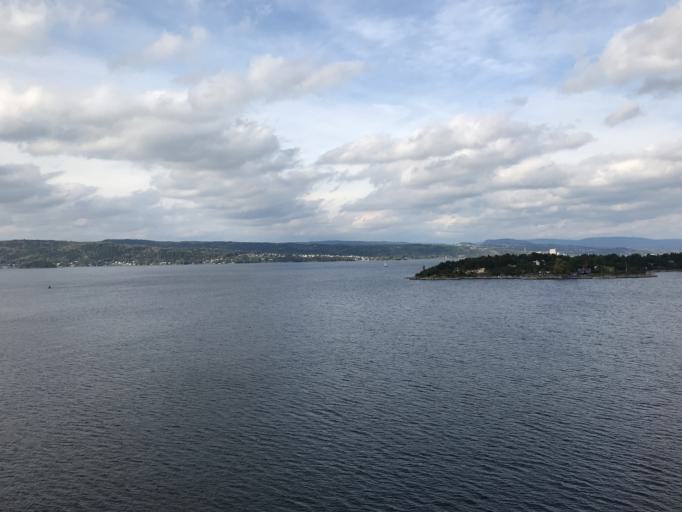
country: NO
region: Akershus
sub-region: Nesodden
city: Fagerstrand
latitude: 59.7455
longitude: 10.5745
